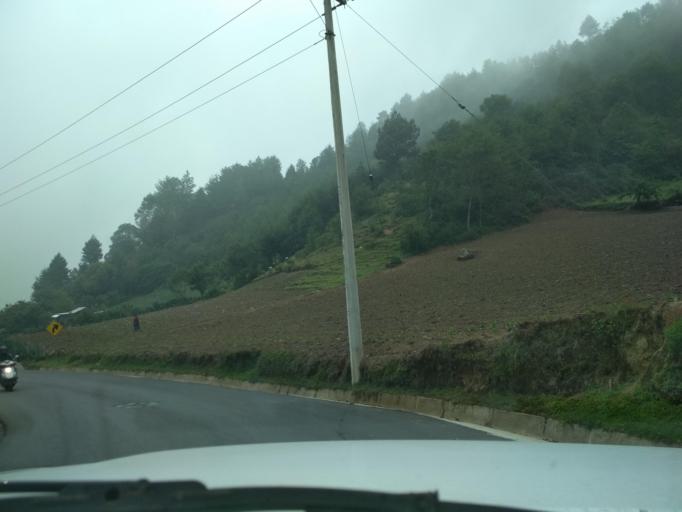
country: MX
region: Veracruz
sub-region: Mariano Escobedo
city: San Isidro el Berro
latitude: 18.9463
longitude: -97.2027
